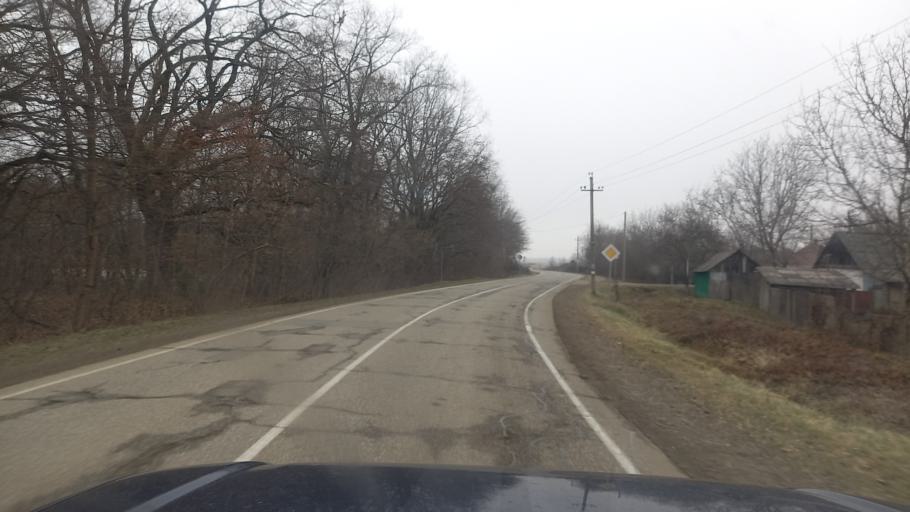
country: RU
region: Krasnodarskiy
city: Neftegorsk
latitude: 44.2914
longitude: 39.8245
